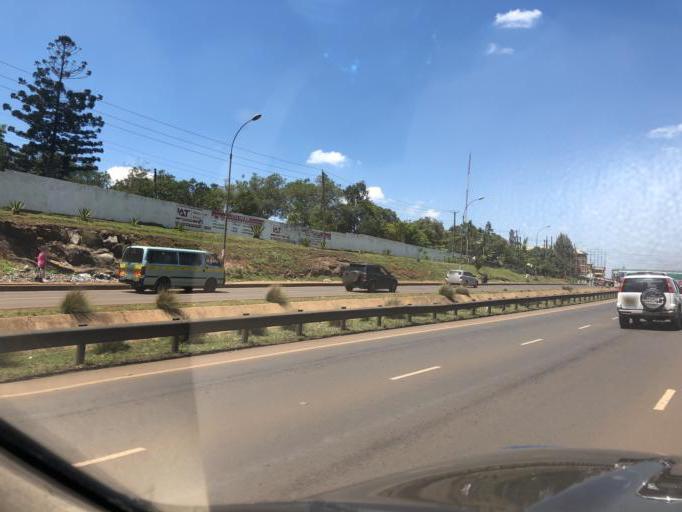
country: KE
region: Kiambu
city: Kiambu
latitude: -1.2149
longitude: 36.8969
